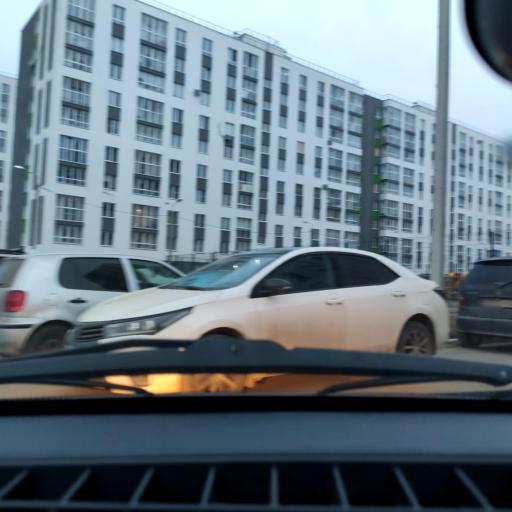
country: RU
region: Bashkortostan
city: Ufa
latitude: 54.6893
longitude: 55.9699
